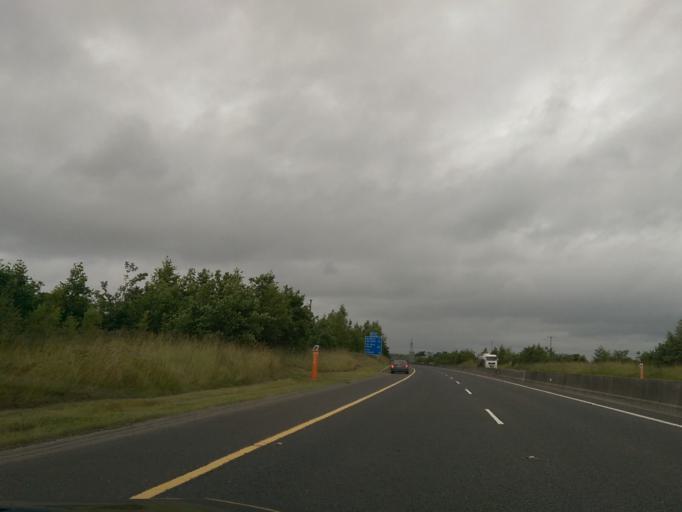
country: IE
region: Munster
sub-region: An Clar
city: Newmarket on Fergus
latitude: 52.7980
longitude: -8.9226
